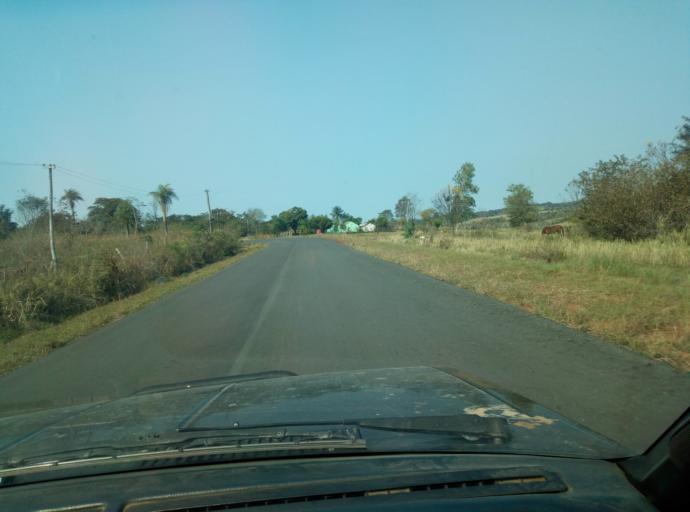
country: PY
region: Caaguazu
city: Carayao
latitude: -25.1866
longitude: -56.3125
